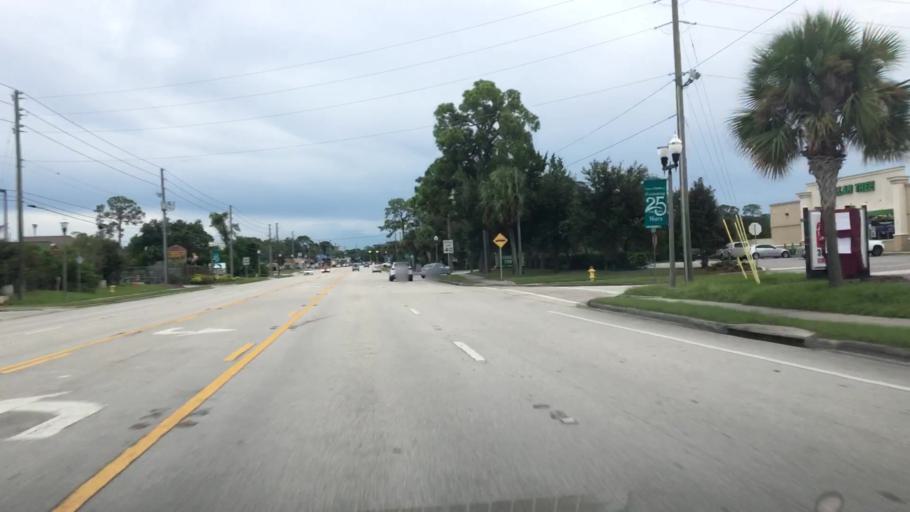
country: US
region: Florida
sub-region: Volusia County
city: DeBary
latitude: 28.8865
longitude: -81.3079
